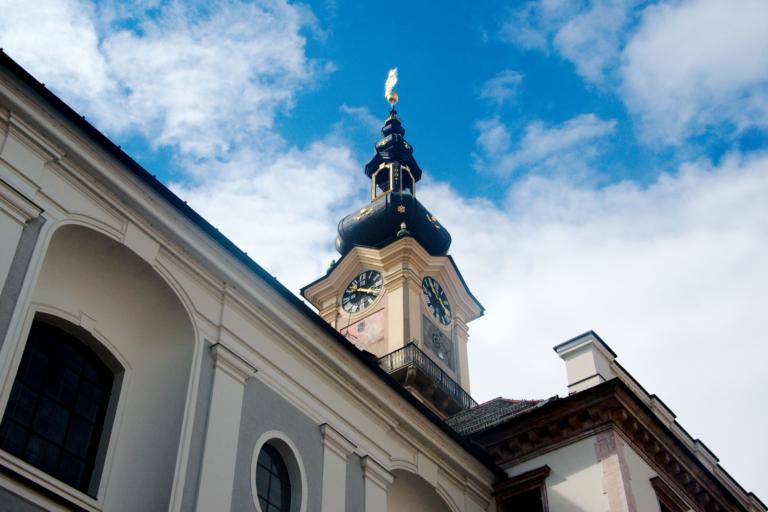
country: AT
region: Upper Austria
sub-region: Linz Stadt
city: Linz
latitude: 48.3043
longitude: 14.2854
